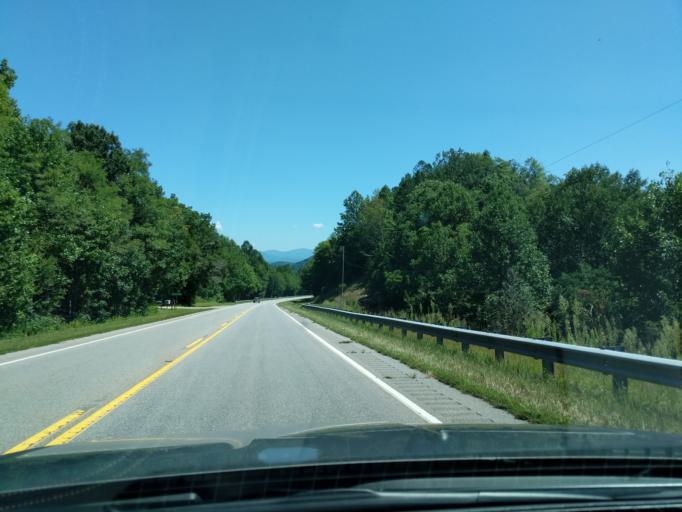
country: US
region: North Carolina
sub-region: Macon County
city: Franklin
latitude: 35.1372
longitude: -83.5041
